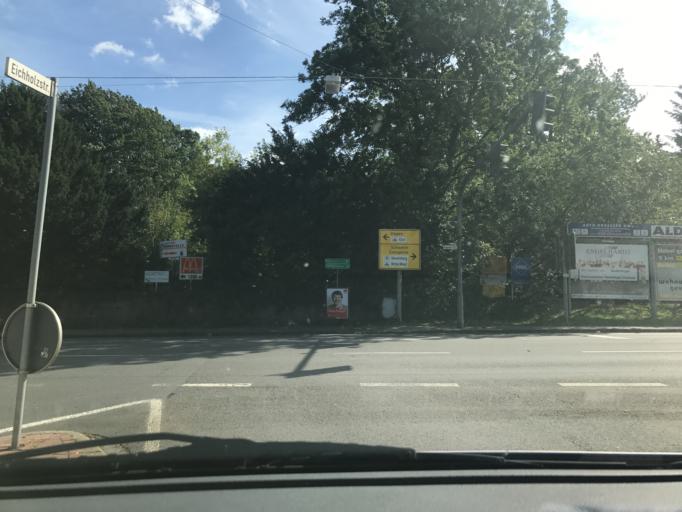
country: DE
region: North Rhine-Westphalia
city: Gevelsberg
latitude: 51.3300
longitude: 7.3697
